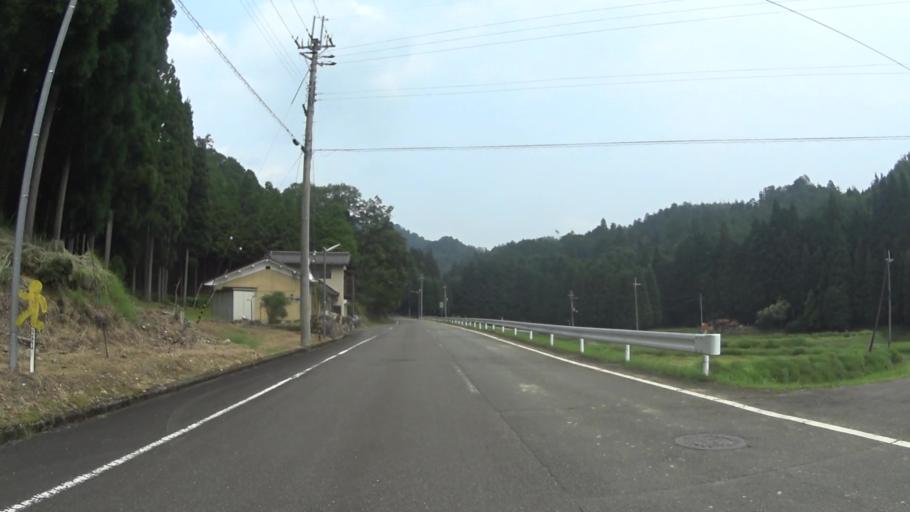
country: JP
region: Kyoto
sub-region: Kyoto-shi
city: Kamigyo-ku
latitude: 35.2045
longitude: 135.6566
